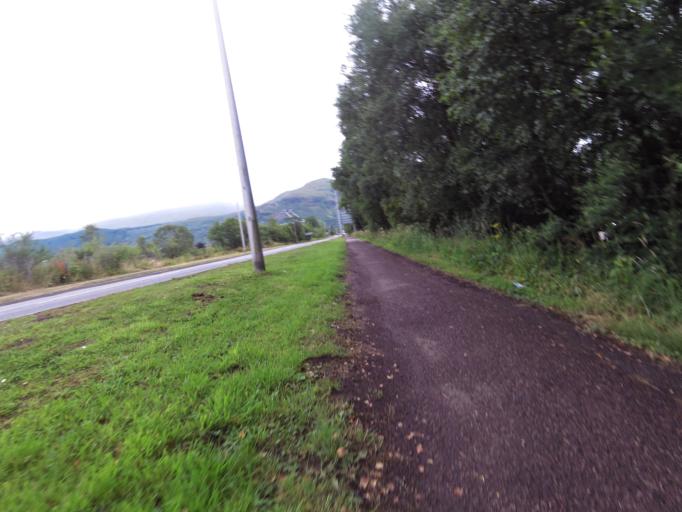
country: GB
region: Scotland
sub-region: Highland
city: Fort William
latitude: 56.8395
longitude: -5.0837
